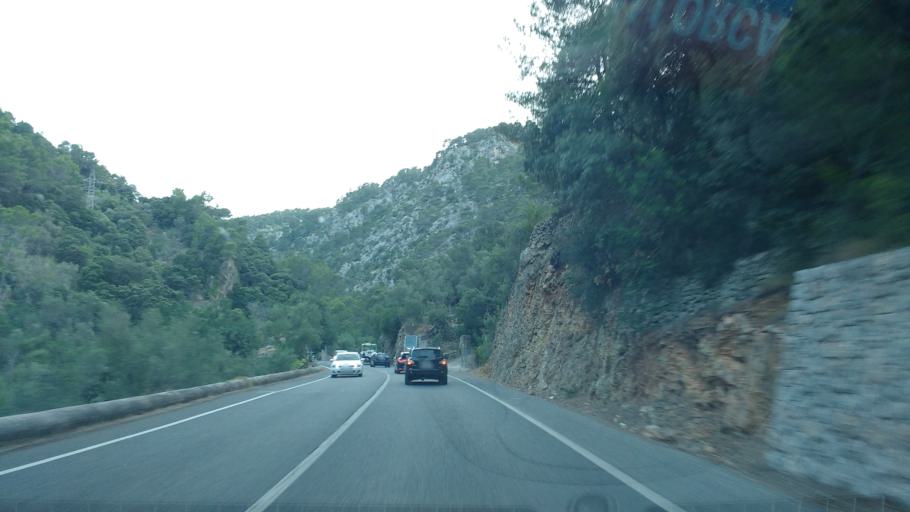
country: ES
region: Balearic Islands
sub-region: Illes Balears
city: Soller
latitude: 39.7489
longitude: 2.7022
